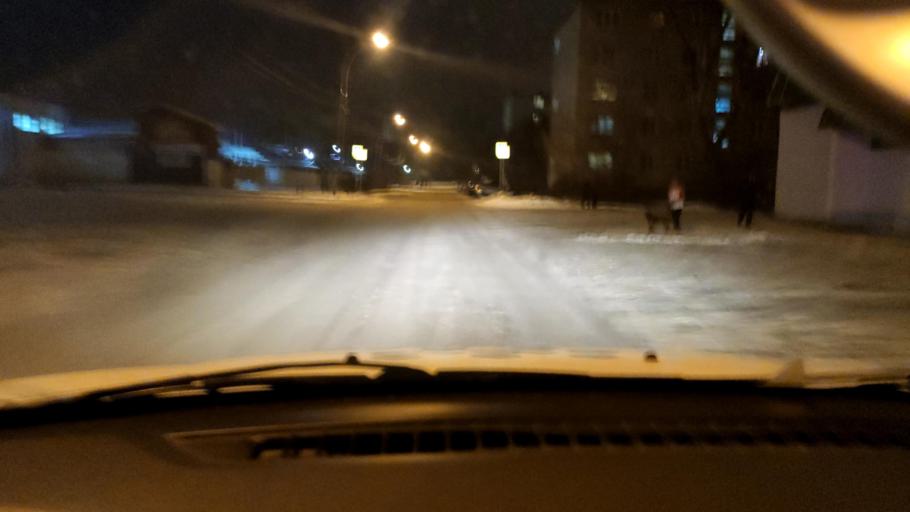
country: RU
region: Perm
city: Overyata
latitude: 58.0088
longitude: 55.9381
